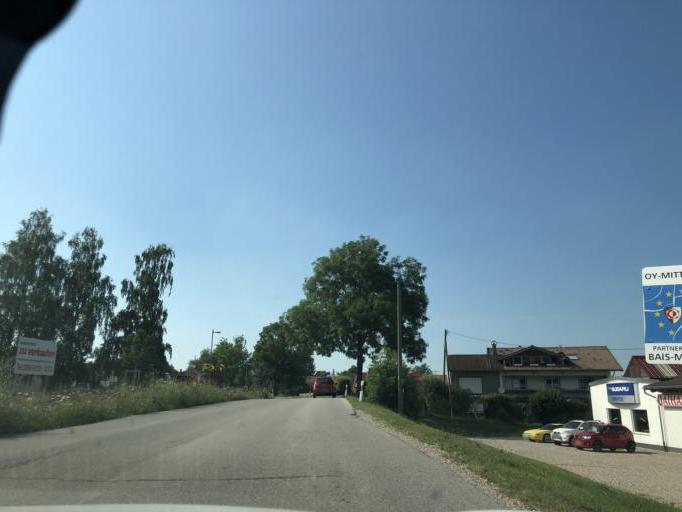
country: DE
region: Bavaria
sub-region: Swabia
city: Oy-Mittelberg
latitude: 47.6411
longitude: 10.4579
